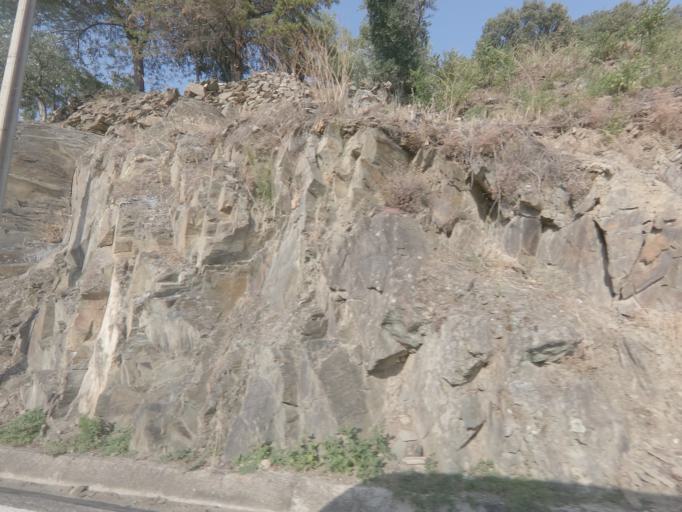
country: PT
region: Viseu
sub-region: Tabuaco
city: Tabuaco
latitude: 41.1355
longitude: -7.5333
